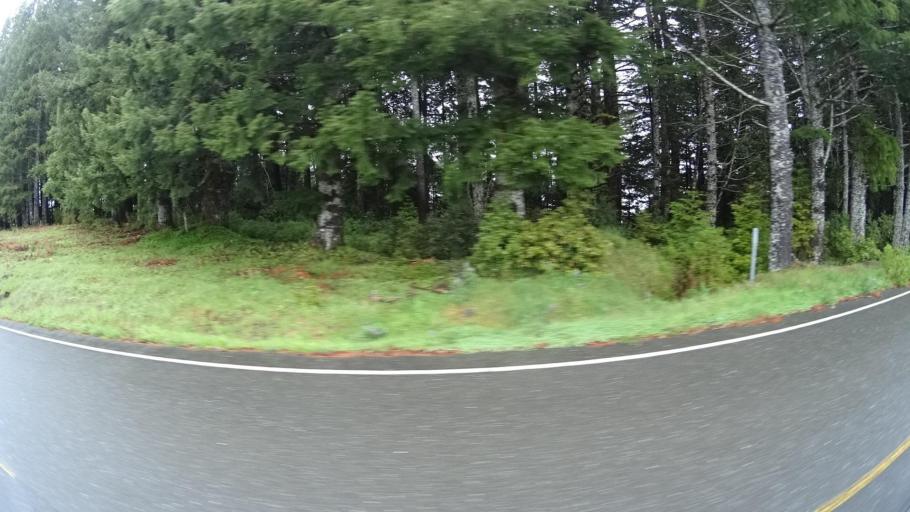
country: US
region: California
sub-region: Humboldt County
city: Westhaven-Moonstone
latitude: 41.1925
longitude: -123.9379
